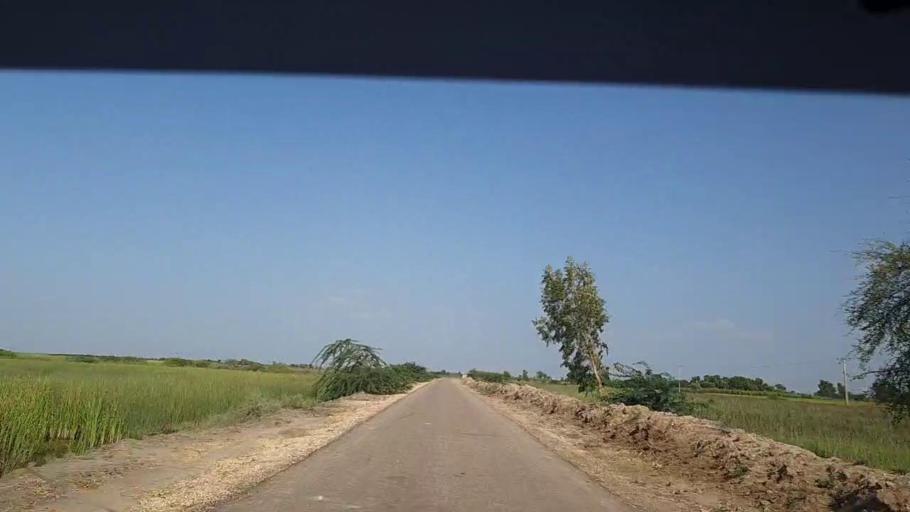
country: PK
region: Sindh
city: Kadhan
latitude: 24.4652
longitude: 68.8350
